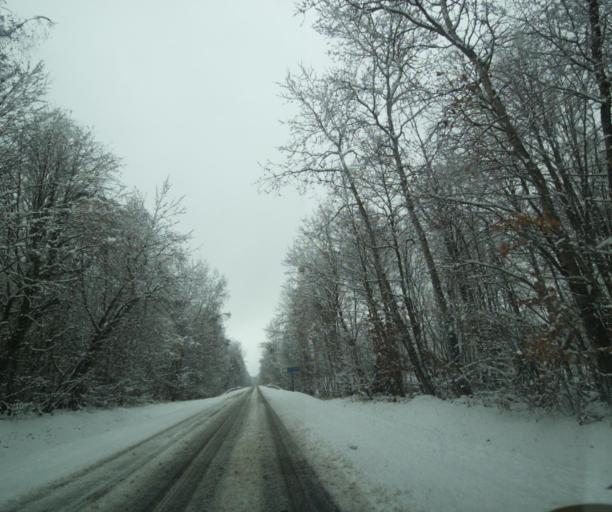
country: FR
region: Champagne-Ardenne
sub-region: Departement de la Haute-Marne
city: Montier-en-Der
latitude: 48.5287
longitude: 4.7917
